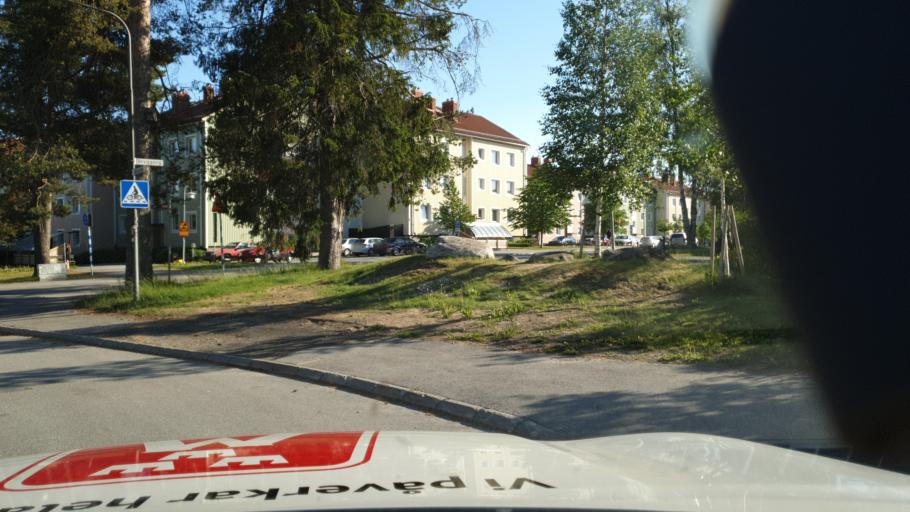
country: SE
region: Vaesterbotten
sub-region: Umea Kommun
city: Umea
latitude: 63.8198
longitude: 20.2386
